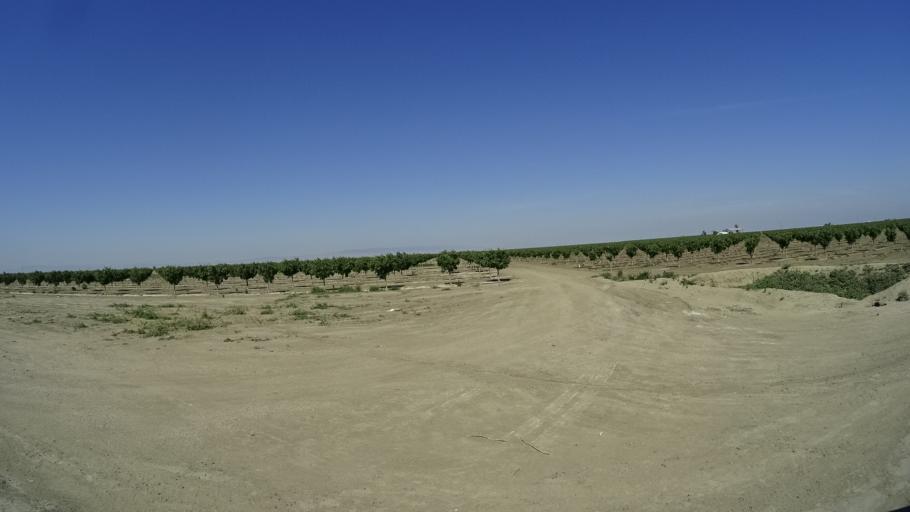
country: US
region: California
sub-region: Fresno County
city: Riverdale
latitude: 36.3826
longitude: -119.9413
